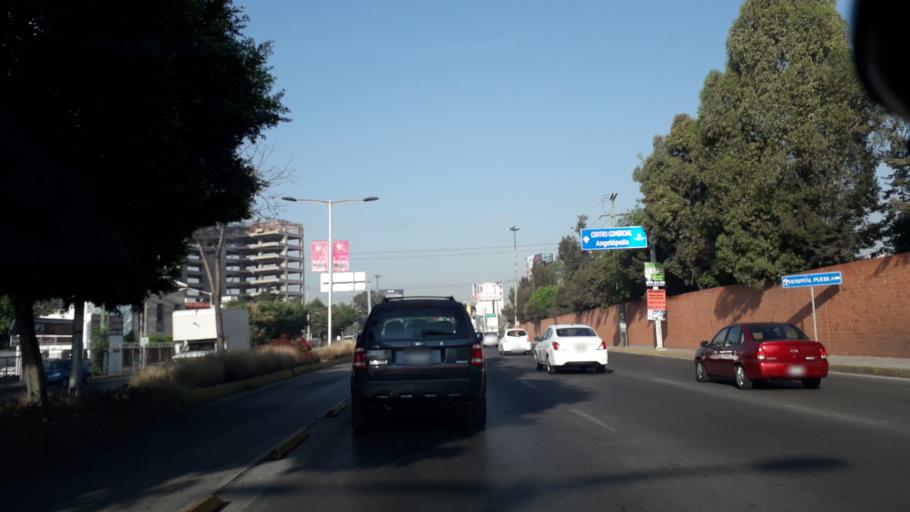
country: MX
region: Puebla
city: Tlazcalancingo
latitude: 19.0388
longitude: -98.2434
